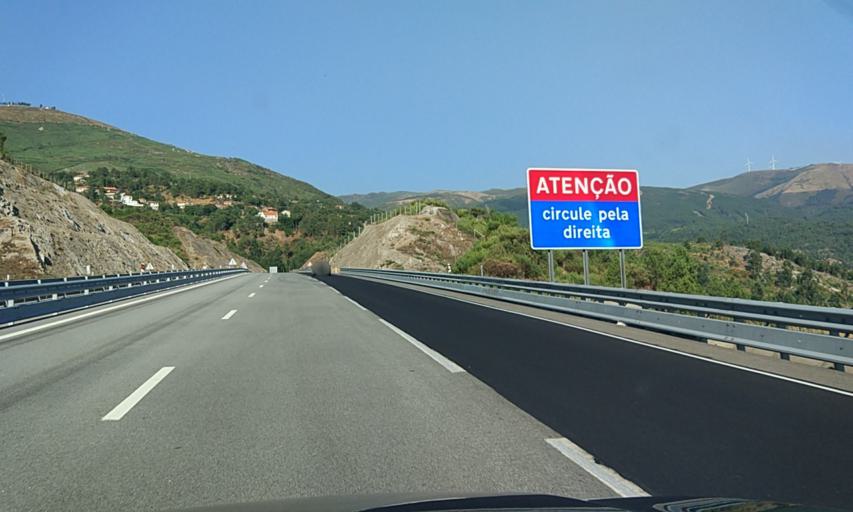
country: PT
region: Porto
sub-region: Amarante
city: Amarante
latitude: 41.2584
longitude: -7.9874
